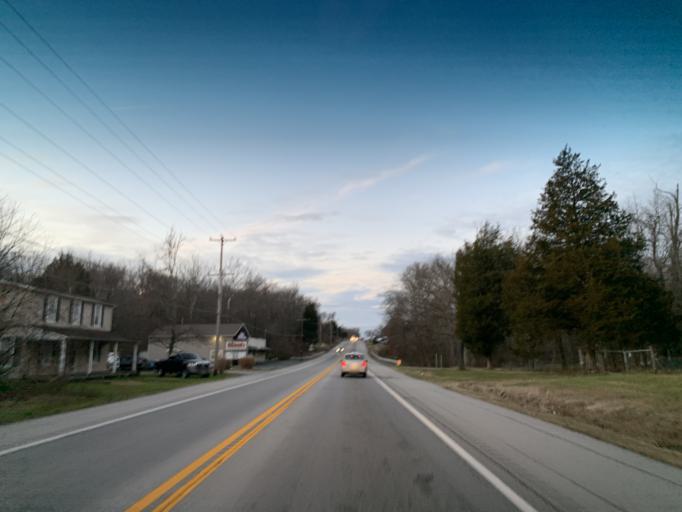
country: US
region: Maryland
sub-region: Cecil County
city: Elkton
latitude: 39.5745
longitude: -75.8164
